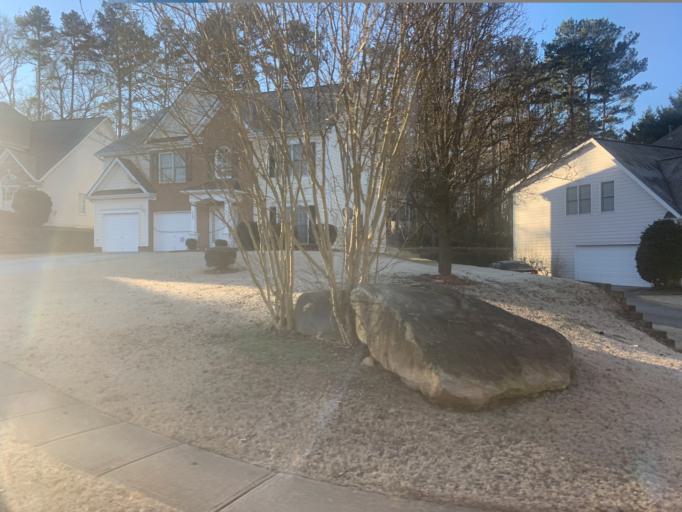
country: US
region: Georgia
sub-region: Gwinnett County
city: Mountain Park
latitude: 33.8690
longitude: -84.1110
